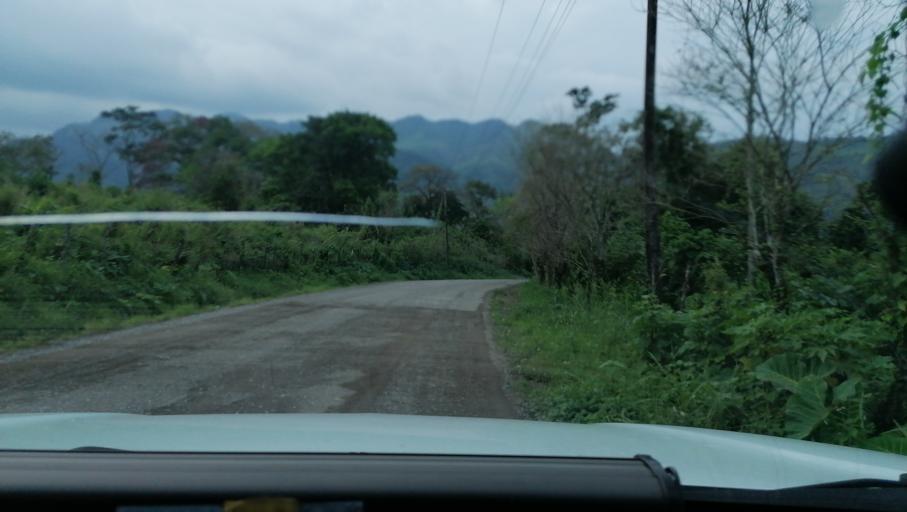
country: MX
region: Chiapas
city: Ixtacomitan
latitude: 17.3473
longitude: -93.1311
